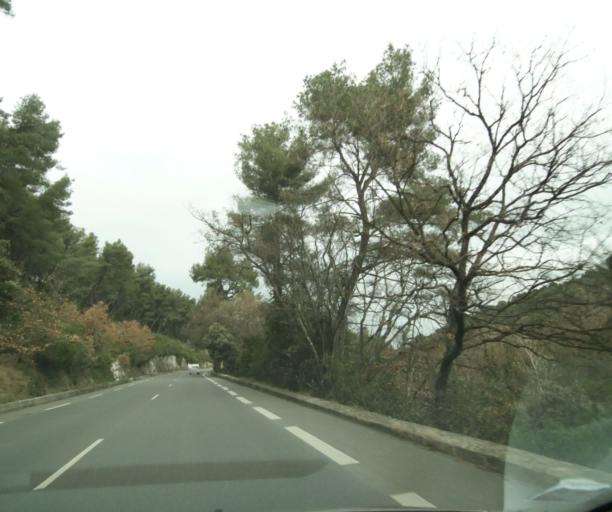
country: FR
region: Provence-Alpes-Cote d'Azur
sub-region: Departement des Bouches-du-Rhone
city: Aix-en-Provence
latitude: 43.5458
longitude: 5.4607
